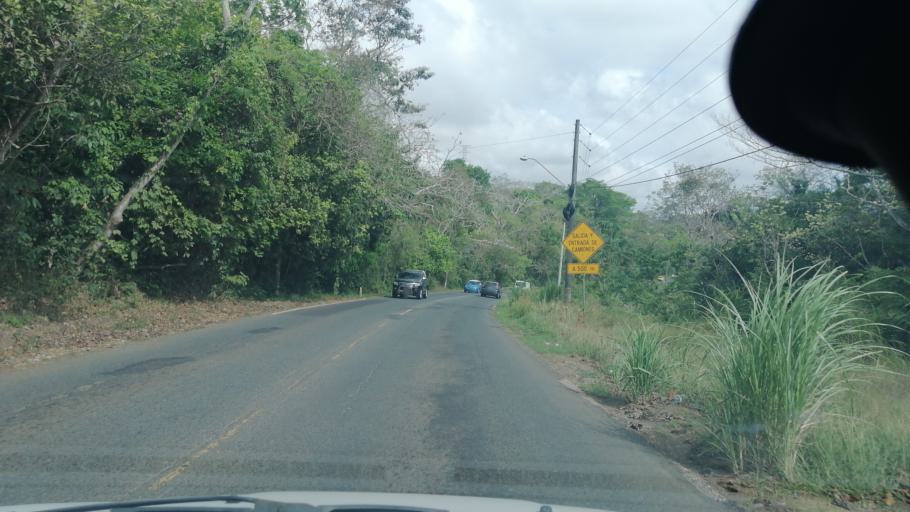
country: PA
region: Panama
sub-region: Distrito de Panama
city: Paraiso
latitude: 9.0405
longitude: -79.6338
